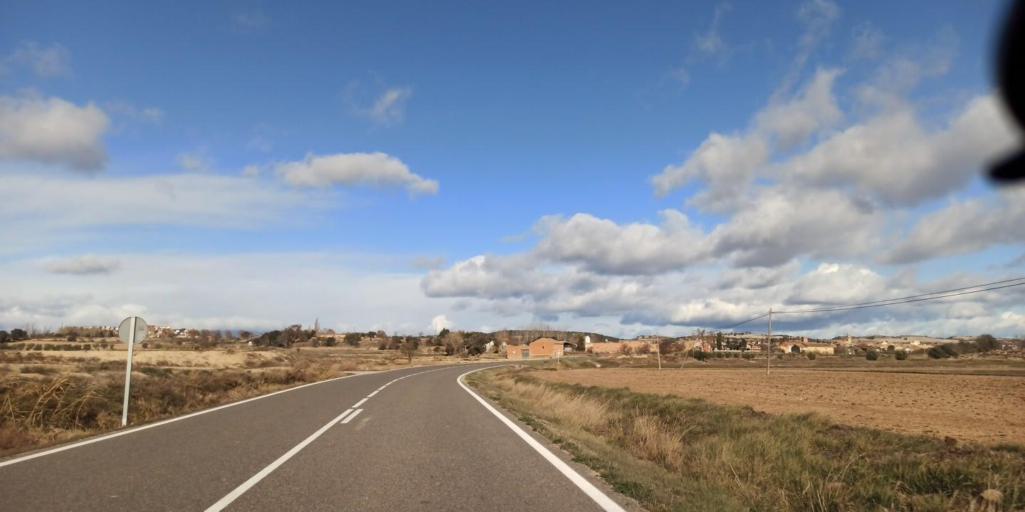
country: ES
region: Catalonia
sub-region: Provincia de Lleida
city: Penelles
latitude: 41.7506
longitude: 0.9548
